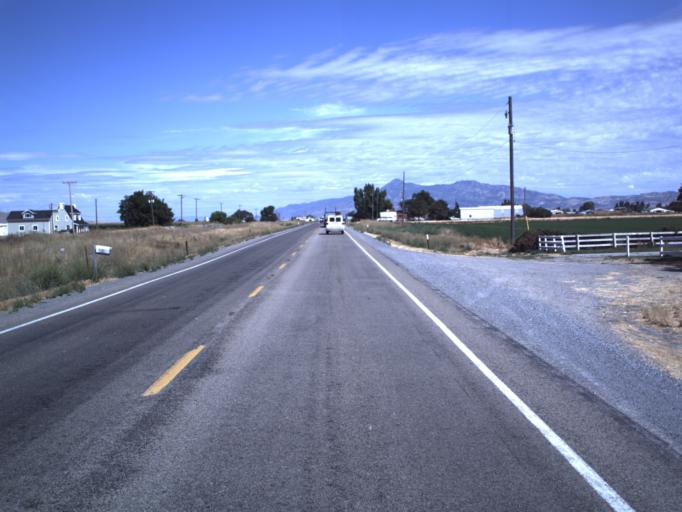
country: US
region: Utah
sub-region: Box Elder County
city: Elwood
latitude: 41.7025
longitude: -112.1419
